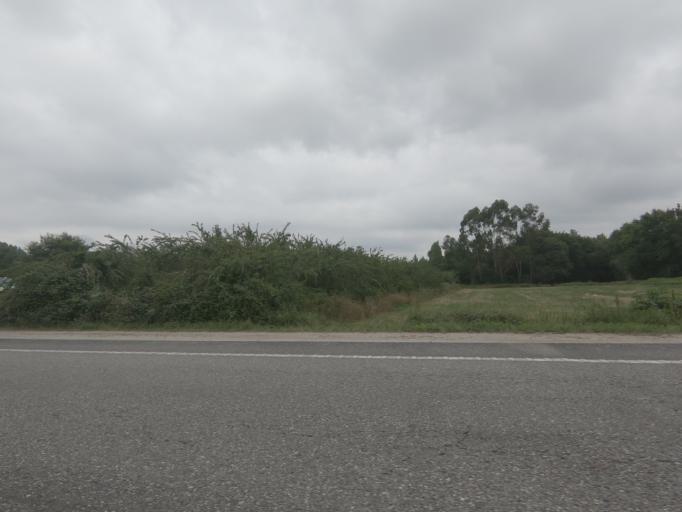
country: PT
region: Viana do Castelo
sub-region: Vila Nova de Cerveira
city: Vila Nova de Cerveira
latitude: 41.9533
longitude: -8.7588
